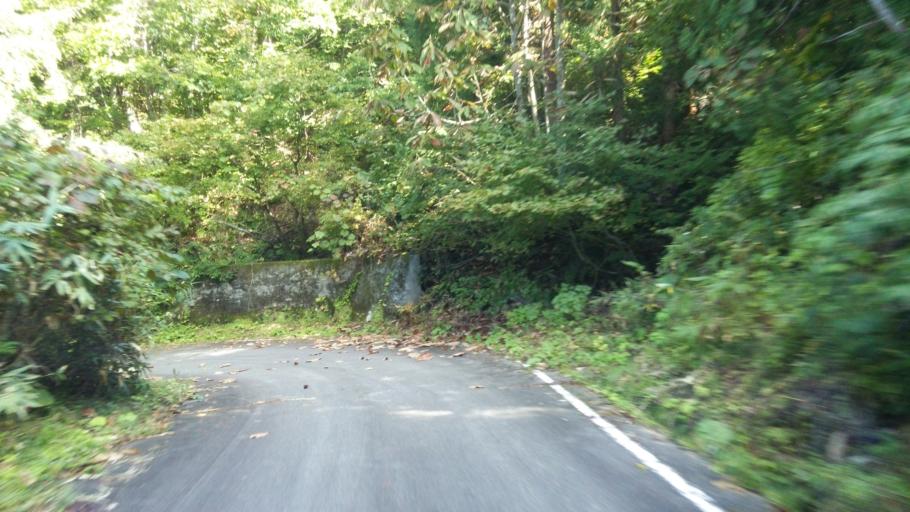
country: JP
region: Fukushima
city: Kitakata
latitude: 37.6121
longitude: 139.9879
